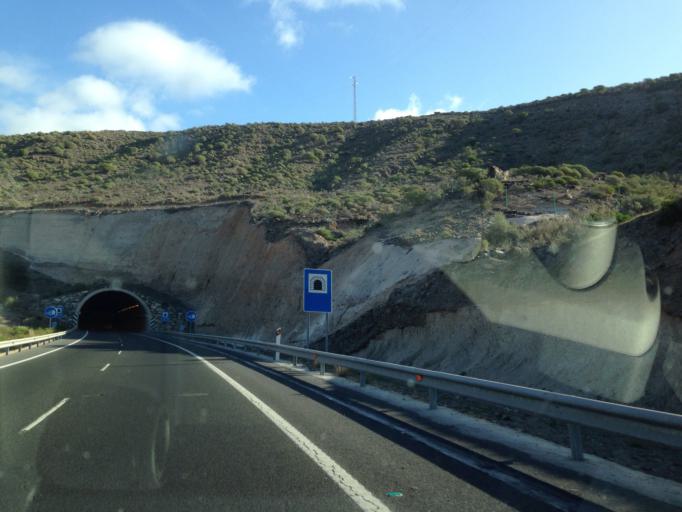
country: ES
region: Canary Islands
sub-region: Provincia de Las Palmas
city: Puerto Rico
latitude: 27.7673
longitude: -15.6630
